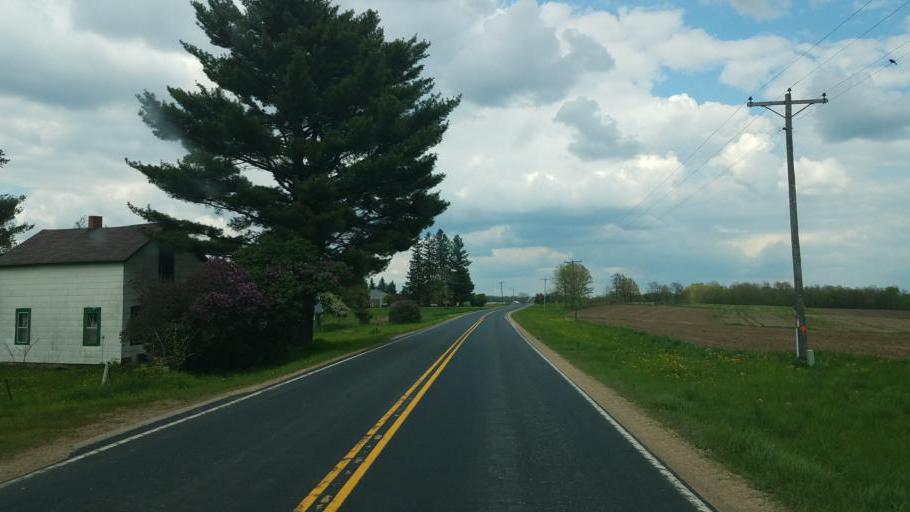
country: US
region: Wisconsin
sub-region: Vernon County
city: Hillsboro
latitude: 43.5903
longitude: -90.3373
